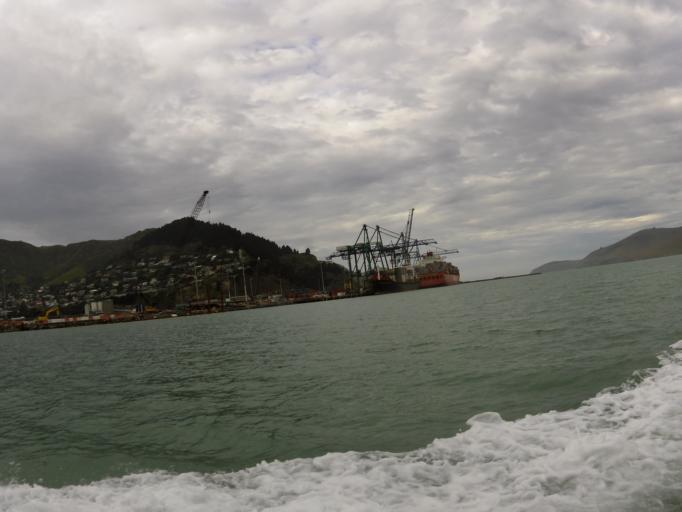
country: NZ
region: Canterbury
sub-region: Christchurch City
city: Christchurch
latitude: -43.6112
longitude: 172.7191
